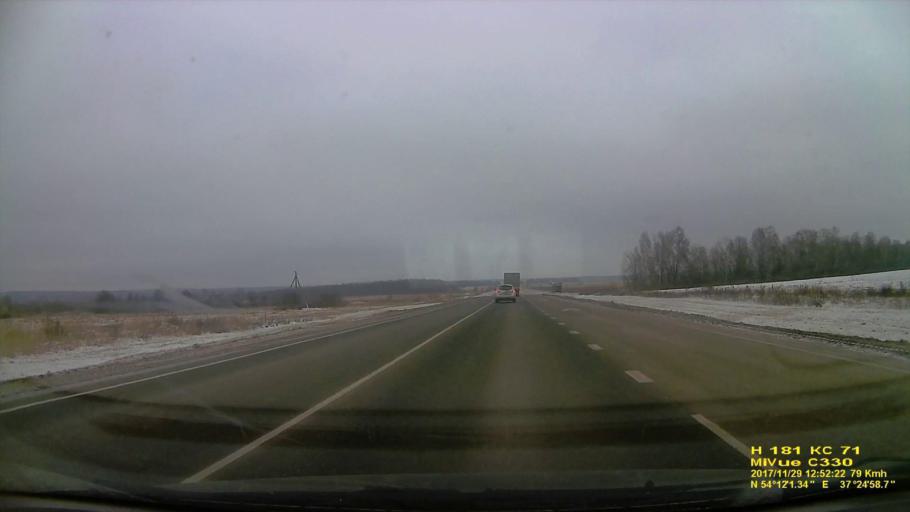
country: RU
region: Tula
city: Barsuki
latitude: 54.2004
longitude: 37.4163
